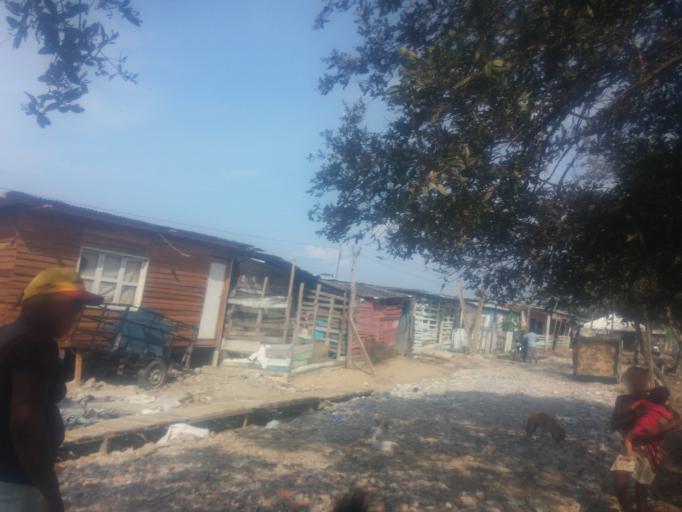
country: CO
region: Bolivar
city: Cartagena
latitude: 10.4146
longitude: -75.4690
